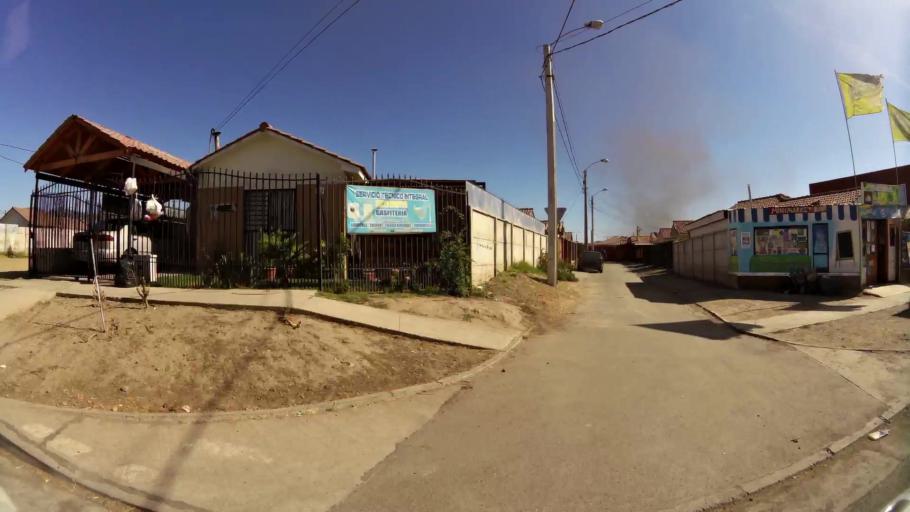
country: CL
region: O'Higgins
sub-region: Provincia de Cachapoal
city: Rancagua
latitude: -34.1846
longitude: -70.7687
